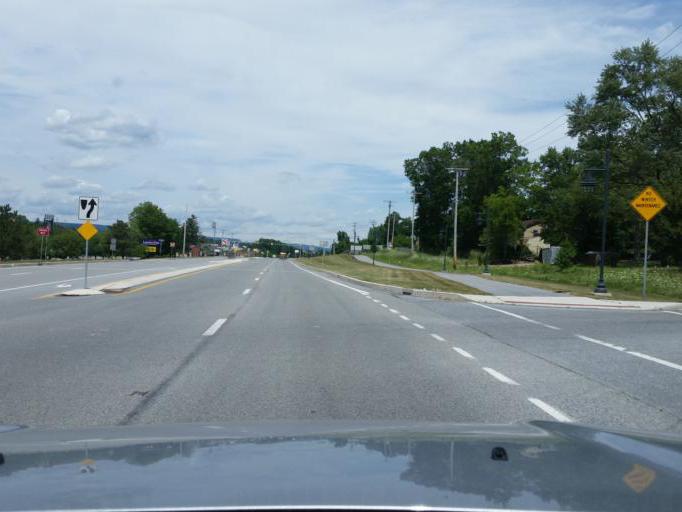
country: US
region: Pennsylvania
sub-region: Blair County
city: Lakemont
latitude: 40.4692
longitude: -78.3925
